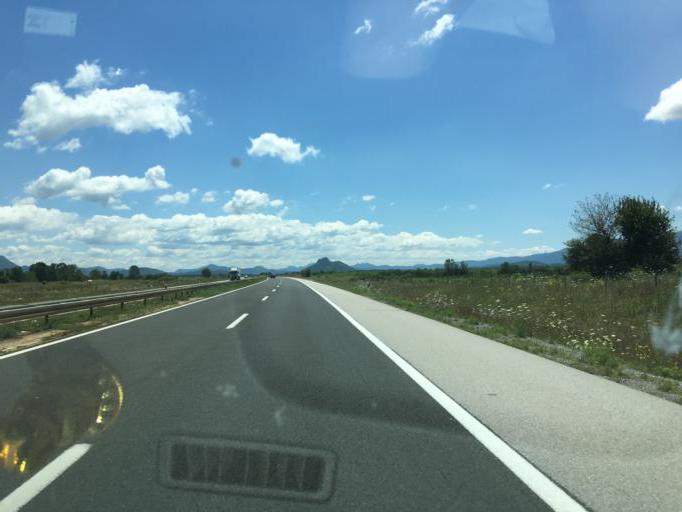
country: HR
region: Licko-Senjska
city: Gospic
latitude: 44.4892
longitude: 15.5432
